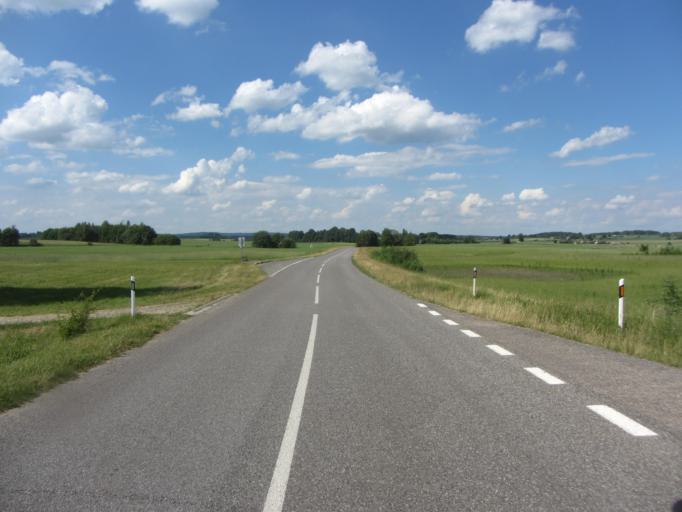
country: LT
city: Aukstadvaris
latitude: 54.5209
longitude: 24.5306
